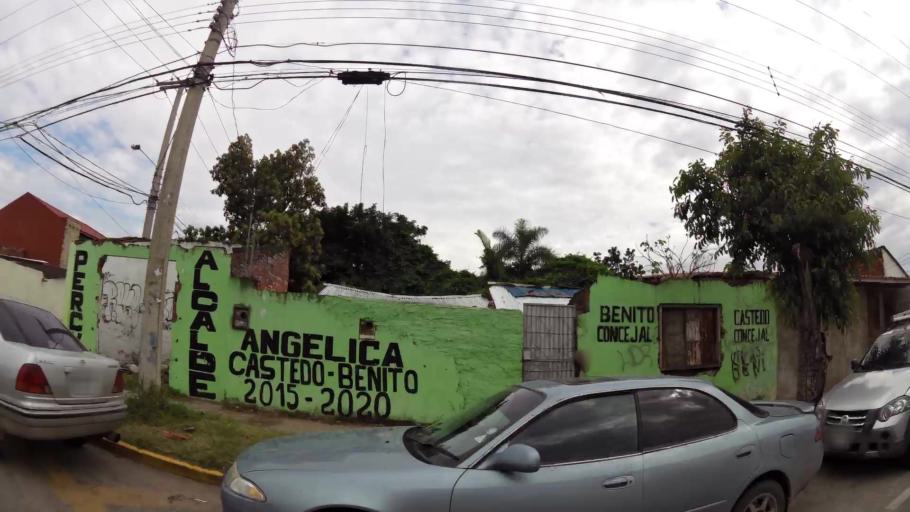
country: BO
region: Santa Cruz
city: Santa Cruz de la Sierra
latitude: -17.7634
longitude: -63.1873
